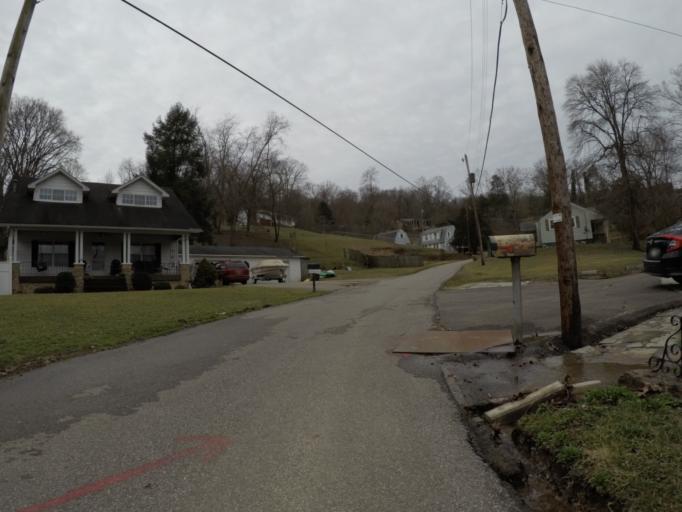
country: US
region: Ohio
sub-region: Lawrence County
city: Burlington
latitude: 38.3925
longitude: -82.5169
